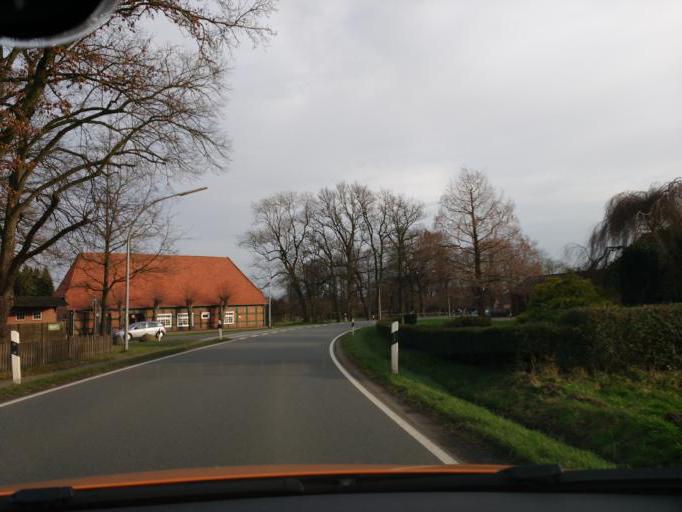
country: DE
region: Lower Saxony
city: Hatten
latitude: 53.0450
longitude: 8.4249
